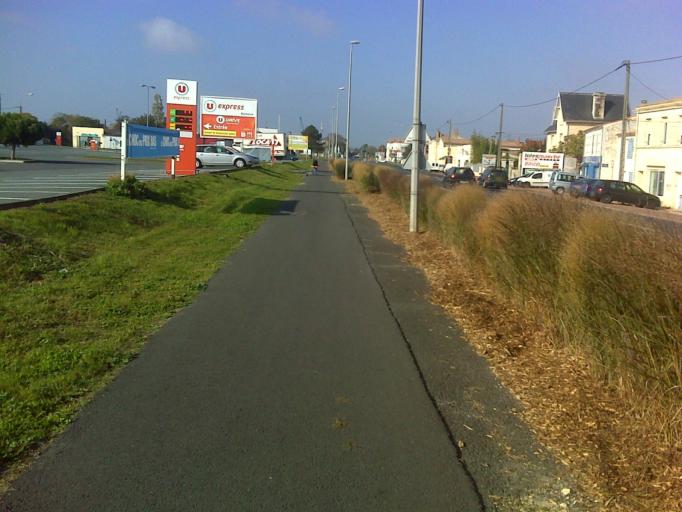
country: FR
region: Poitou-Charentes
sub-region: Departement de la Charente-Maritime
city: Breuil-Magne
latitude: 45.9504
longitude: -0.9418
